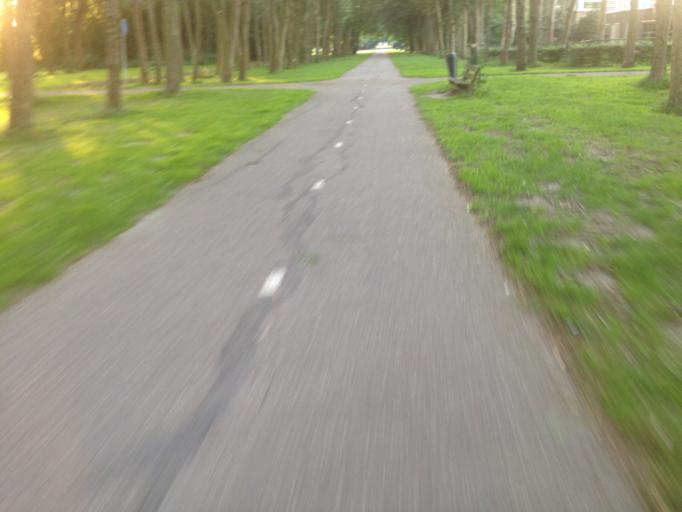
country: NL
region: Flevoland
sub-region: Gemeente Almere
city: Almere Stad
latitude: 52.3905
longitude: 5.2930
